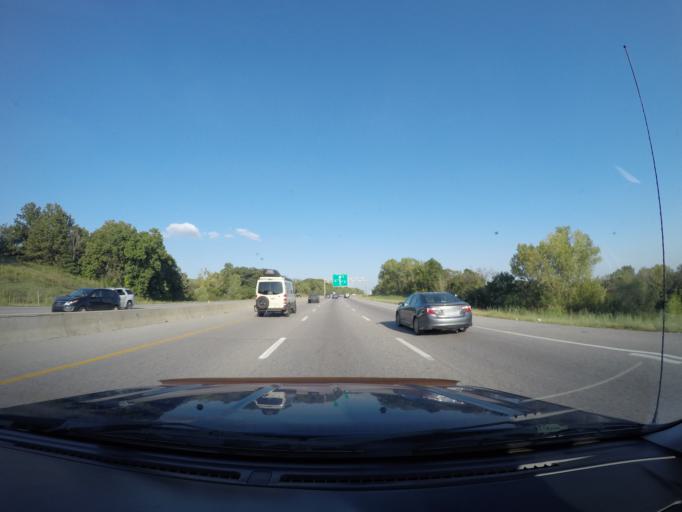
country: US
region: Kansas
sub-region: Johnson County
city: Shawnee
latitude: 39.1059
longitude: -94.7029
